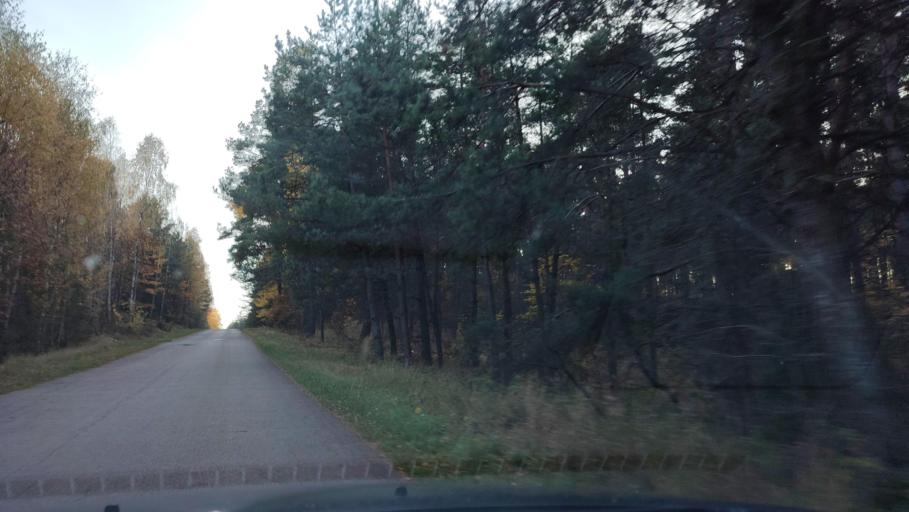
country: PL
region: Masovian Voivodeship
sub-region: Powiat mlawski
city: Dzierzgowo
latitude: 53.2993
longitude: 20.6646
